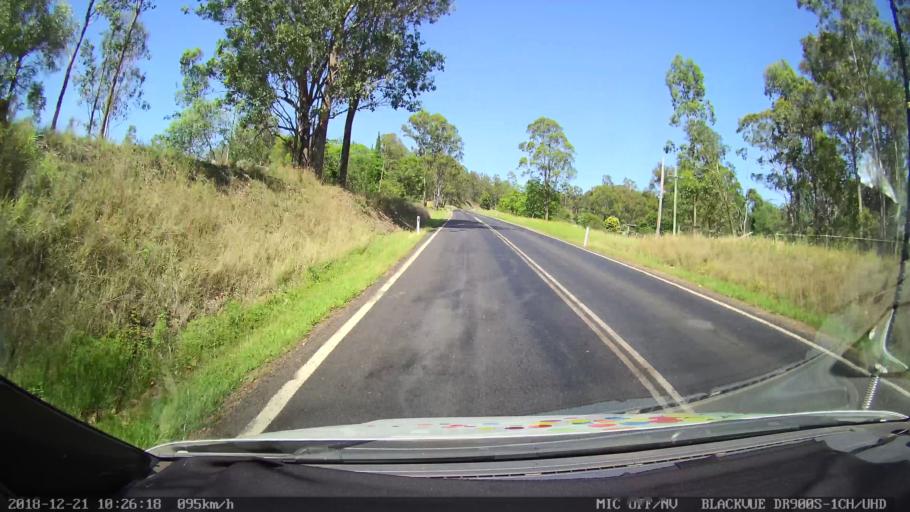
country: AU
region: New South Wales
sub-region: Clarence Valley
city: South Grafton
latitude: -29.6293
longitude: 152.7530
